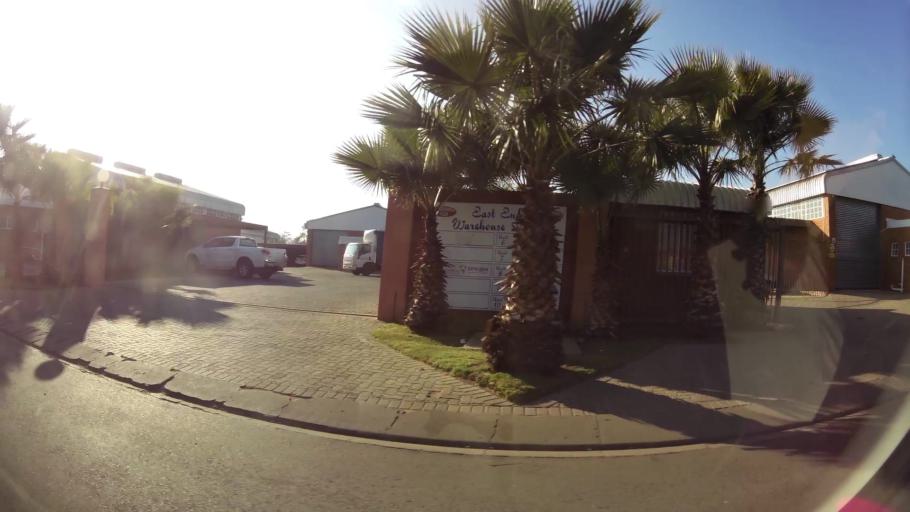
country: ZA
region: Orange Free State
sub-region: Mangaung Metropolitan Municipality
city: Bloemfontein
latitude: -29.1321
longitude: 26.2657
